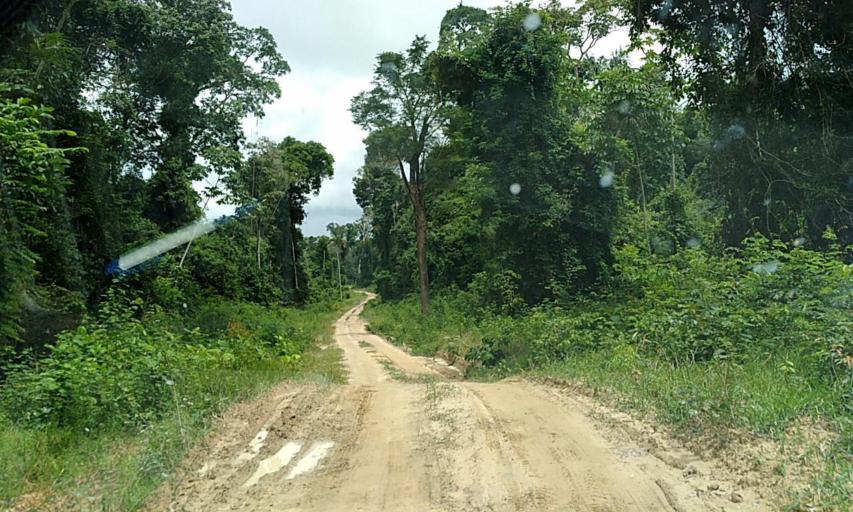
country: BR
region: Para
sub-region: Altamira
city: Altamira
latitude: -3.0535
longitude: -52.9097
